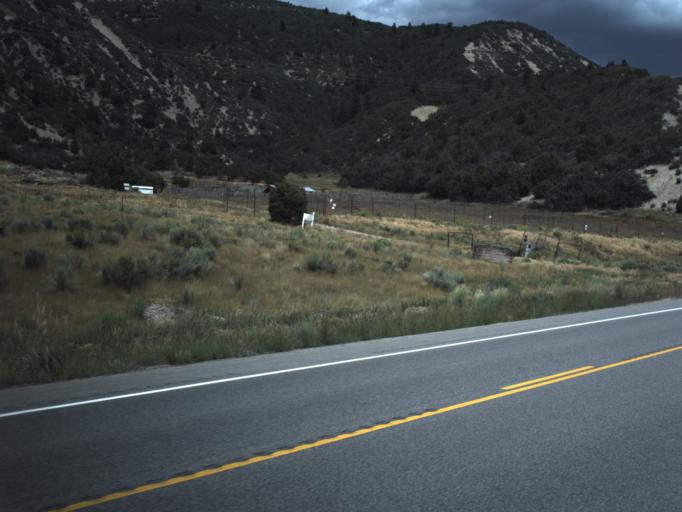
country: US
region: Utah
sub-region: Carbon County
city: Helper
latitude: 39.9365
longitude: -111.1388
